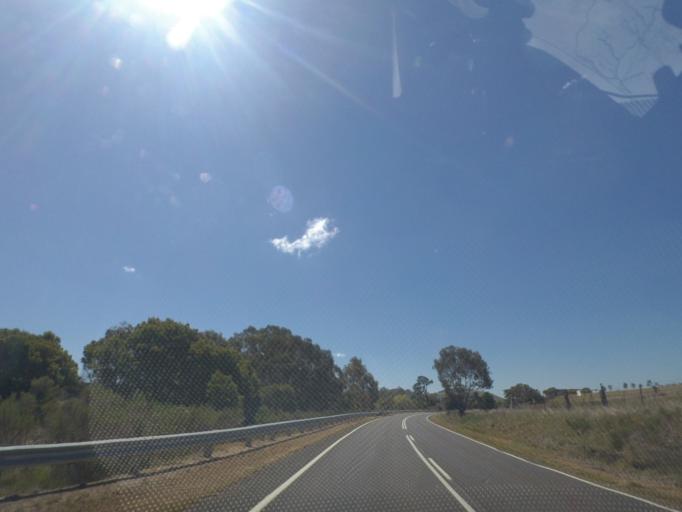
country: AU
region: Victoria
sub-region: Hume
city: Sunbury
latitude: -37.0868
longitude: 144.7591
